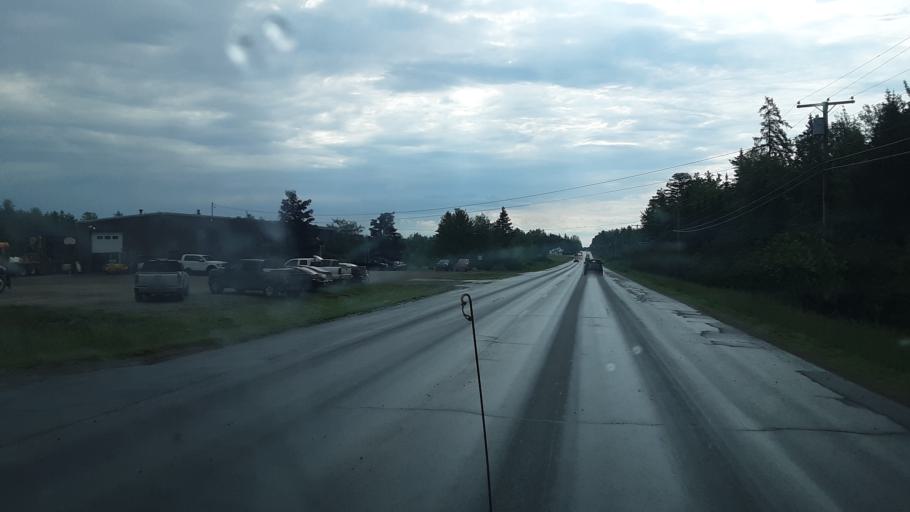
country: US
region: Maine
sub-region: Penobscot County
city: Milford
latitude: 44.9455
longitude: -68.6838
